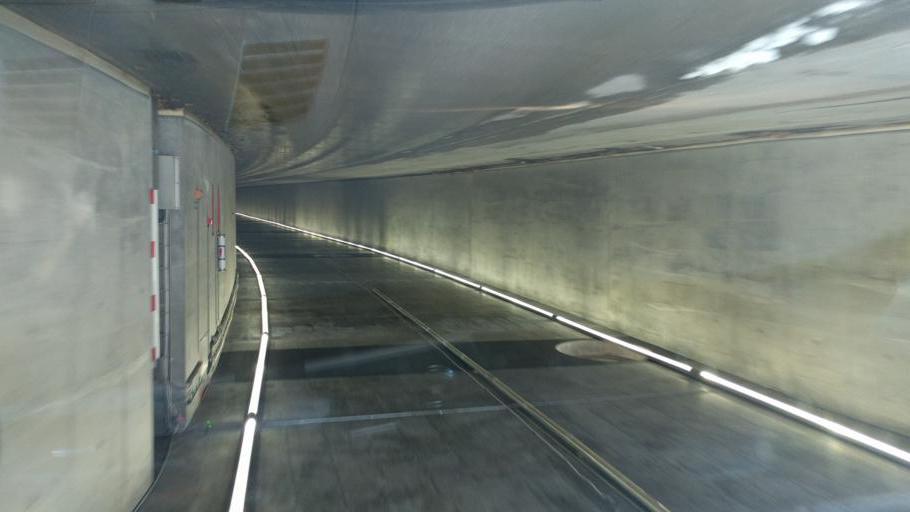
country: SE
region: Stockholm
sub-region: Taby Kommun
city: Taby
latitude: 59.4450
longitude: 18.0751
